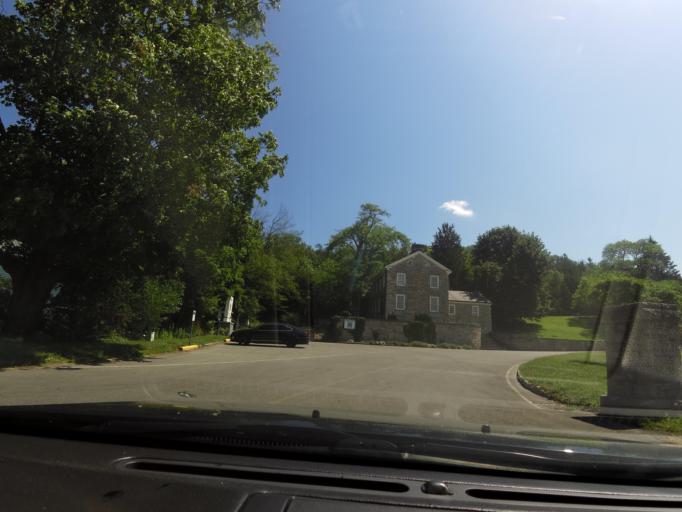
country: US
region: New York
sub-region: Niagara County
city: Lewiston
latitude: 43.1627
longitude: -79.0537
